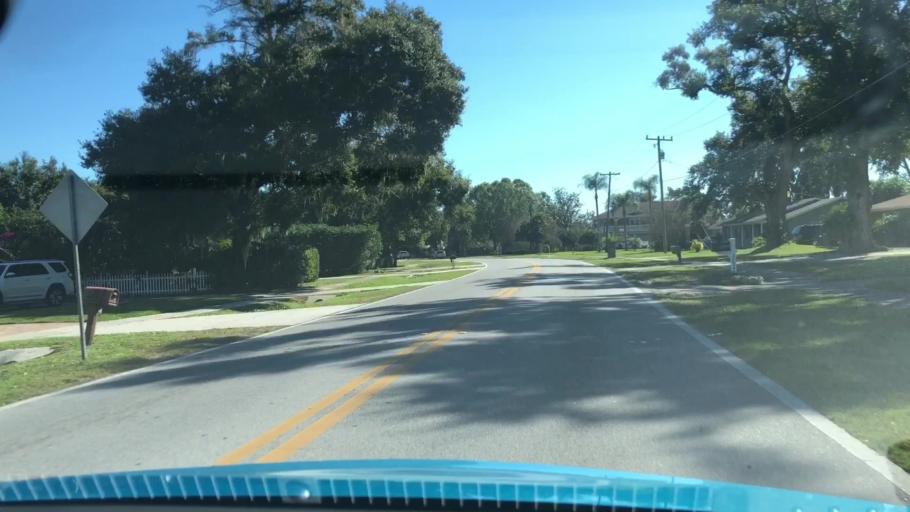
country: US
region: Florida
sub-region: Orange County
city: Pine Castle
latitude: 28.4826
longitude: -81.3471
